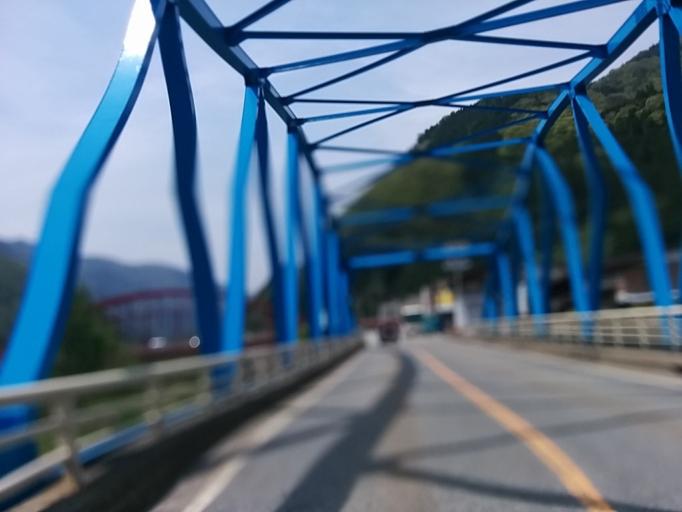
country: JP
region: Gifu
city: Takayama
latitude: 36.2477
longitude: 137.5171
